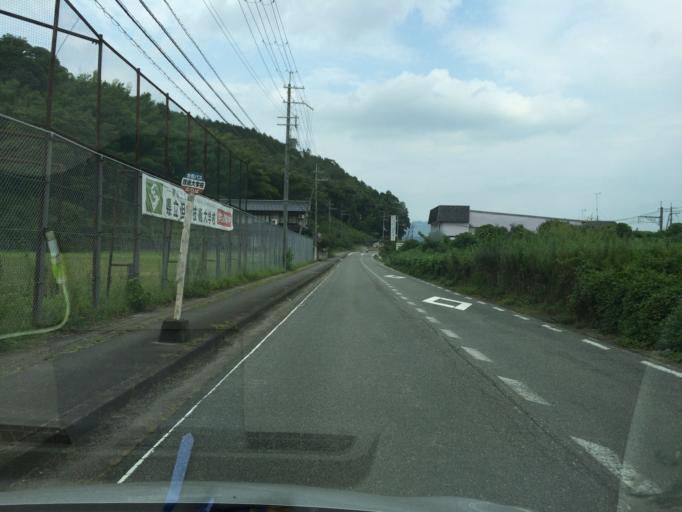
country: JP
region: Hyogo
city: Toyooka
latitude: 35.5174
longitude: 134.8178
